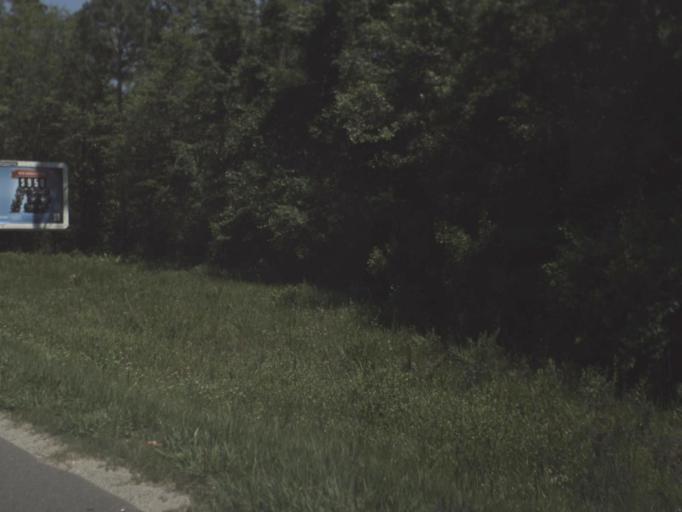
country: US
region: Florida
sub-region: Baker County
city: Macclenny
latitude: 30.2839
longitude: -82.1134
